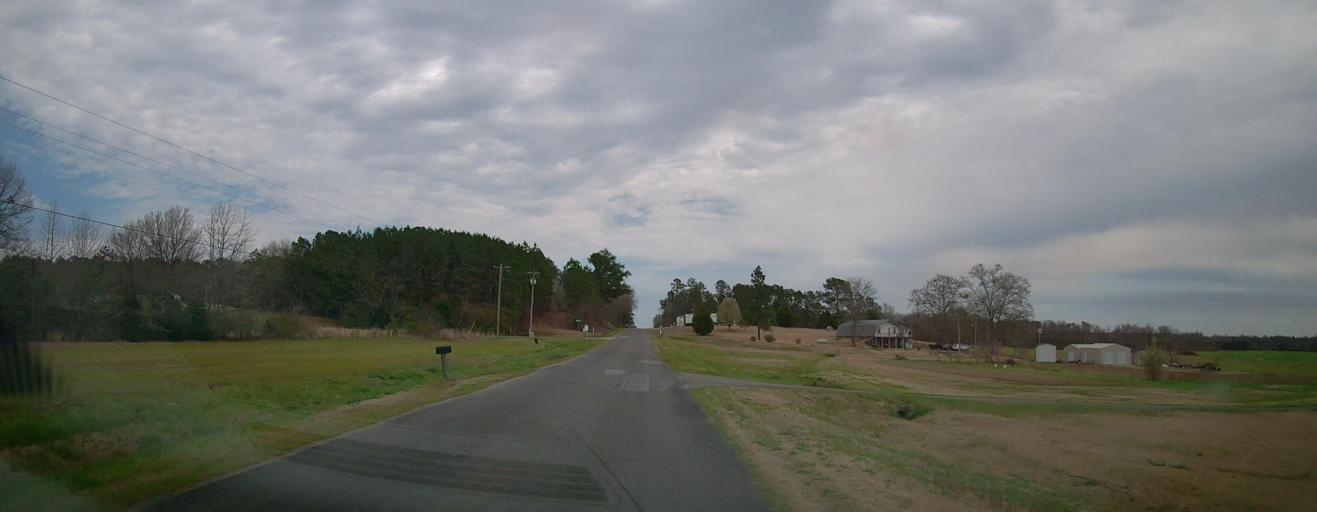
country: US
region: Alabama
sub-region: Marion County
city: Hamilton
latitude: 34.1905
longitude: -88.1492
